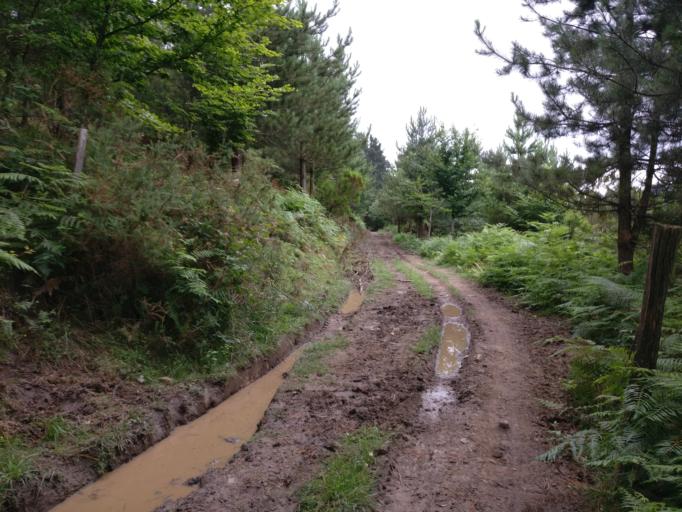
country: ES
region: Basque Country
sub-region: Bizkaia
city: Alonsotegi
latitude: 43.2208
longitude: -2.9489
